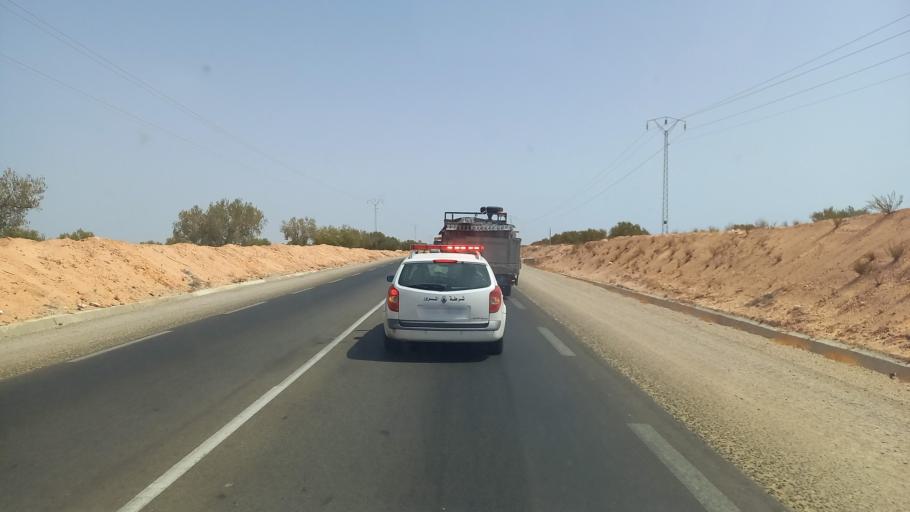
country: TN
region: Madanin
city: Zarzis
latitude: 33.4160
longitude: 10.8721
